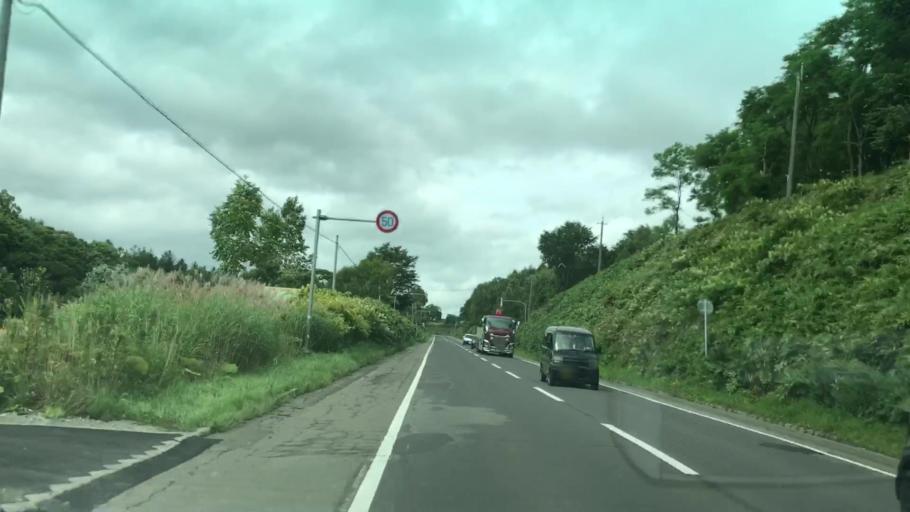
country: JP
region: Hokkaido
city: Niseko Town
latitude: 42.9228
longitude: 140.7363
